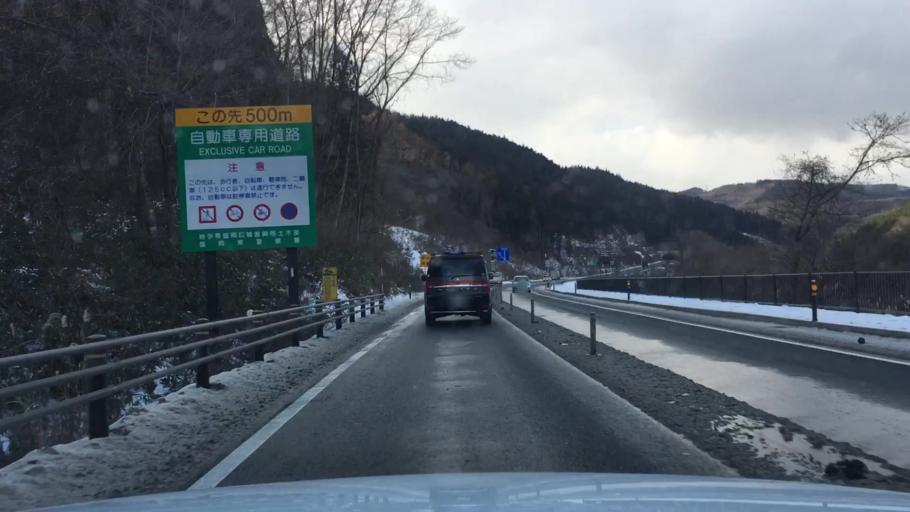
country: JP
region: Iwate
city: Morioka-shi
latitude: 39.6678
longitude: 141.2370
